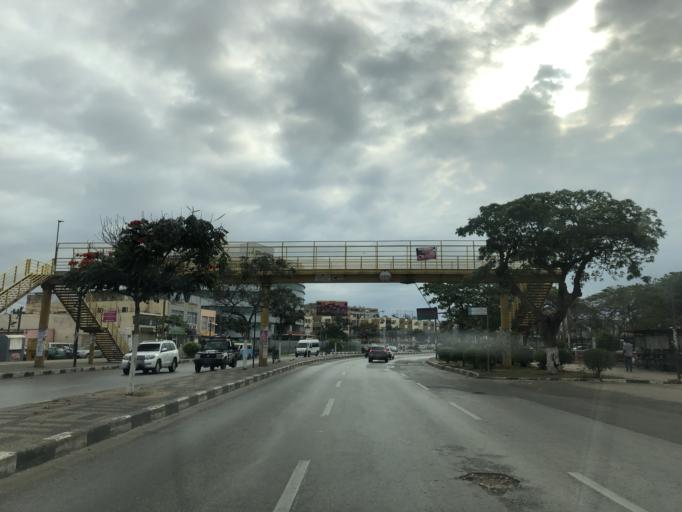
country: AO
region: Luanda
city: Luanda
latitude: -8.8396
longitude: 13.2334
